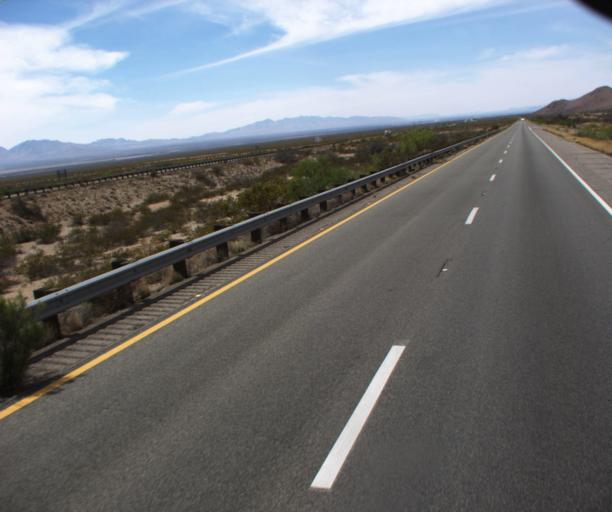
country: US
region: New Mexico
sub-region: Hidalgo County
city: Lordsburg
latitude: 32.2300
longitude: -109.0566
